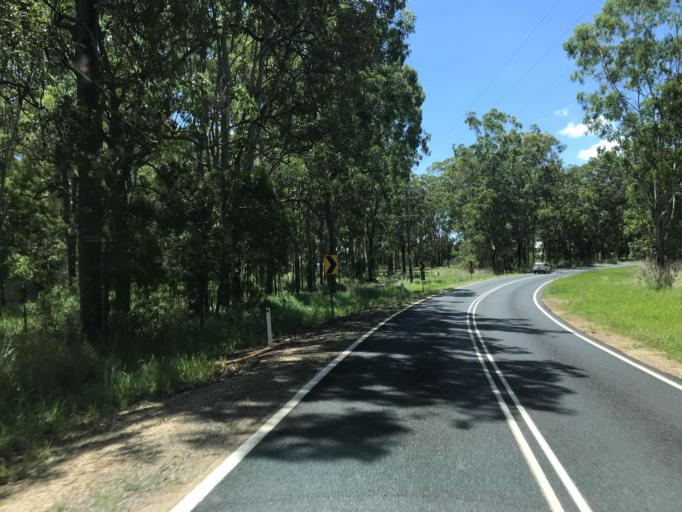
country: AU
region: Queensland
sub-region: Tablelands
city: Atherton
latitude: -17.4299
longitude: 145.4003
